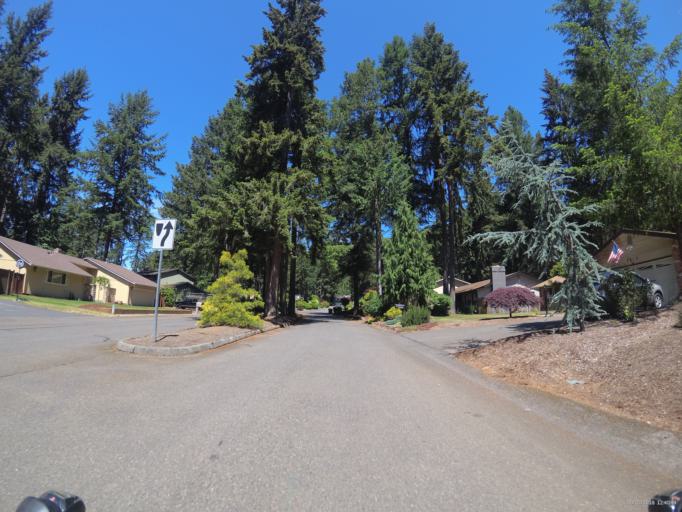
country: US
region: Washington
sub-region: Pierce County
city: University Place
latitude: 47.2025
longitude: -122.5537
